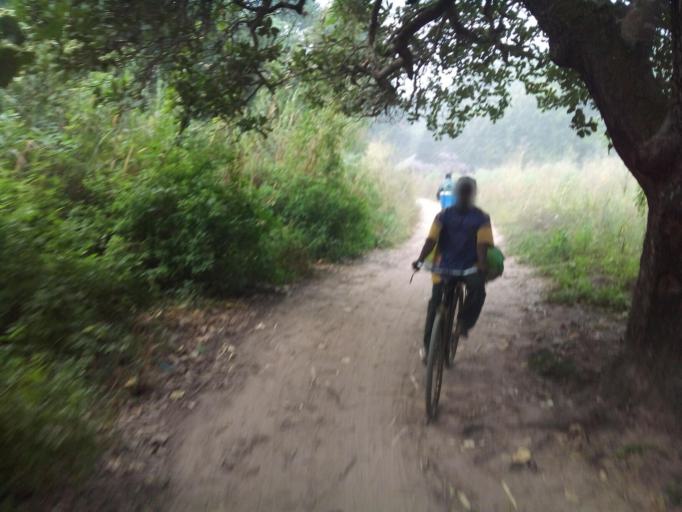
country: MZ
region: Zambezia
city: Quelimane
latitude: -17.5944
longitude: 36.6875
